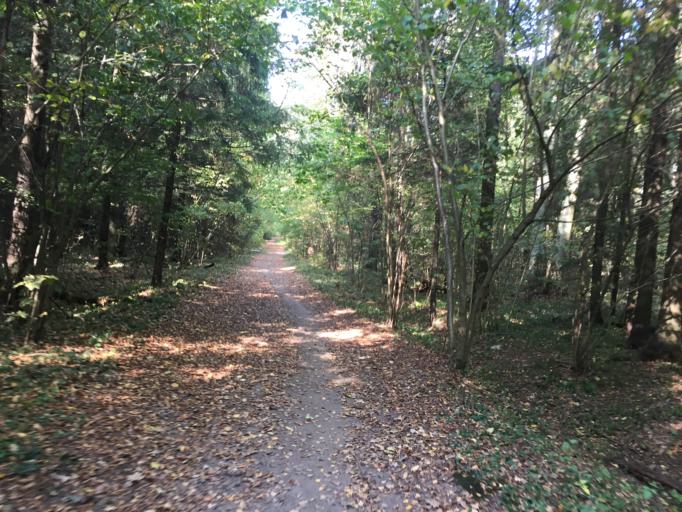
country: RU
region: Moscow
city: Babushkin
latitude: 55.8637
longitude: 37.7429
